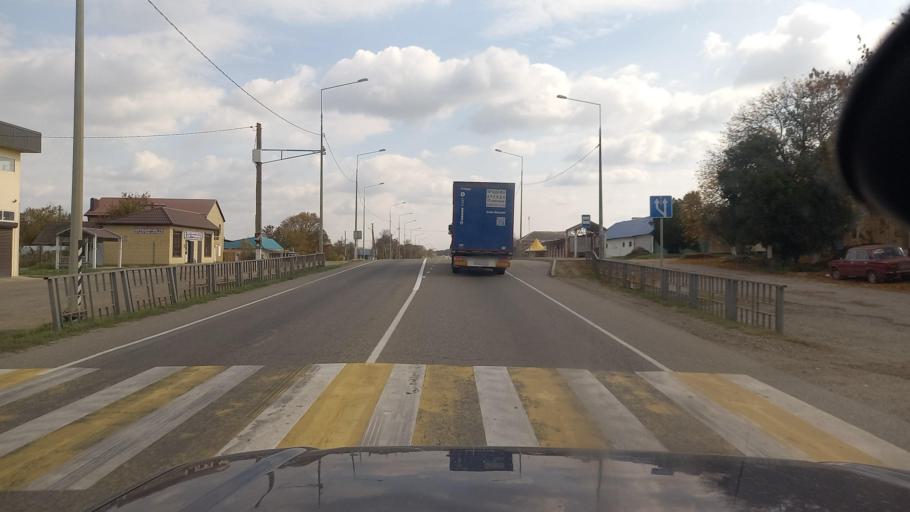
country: RU
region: Krasnodarskiy
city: Kholmskiy
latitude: 44.8481
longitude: 38.4110
